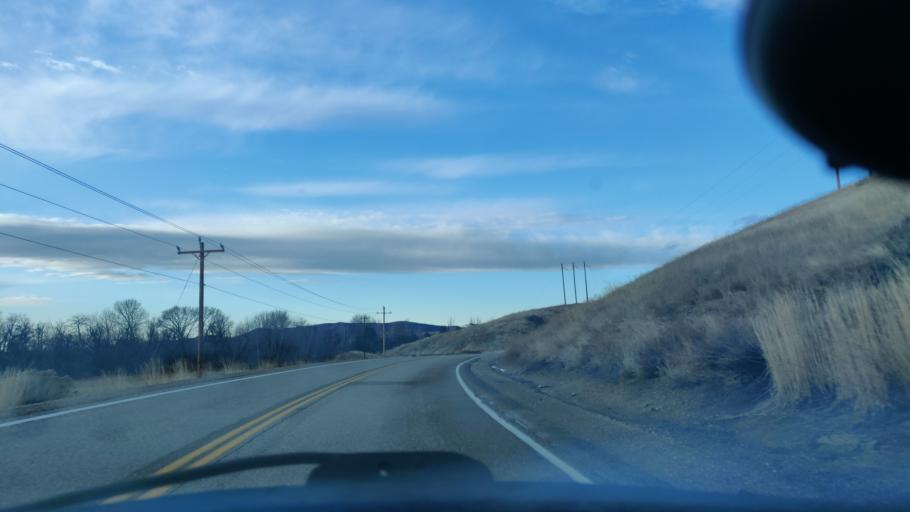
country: US
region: Idaho
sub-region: Ada County
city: Garden City
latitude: 43.7262
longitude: -116.2497
